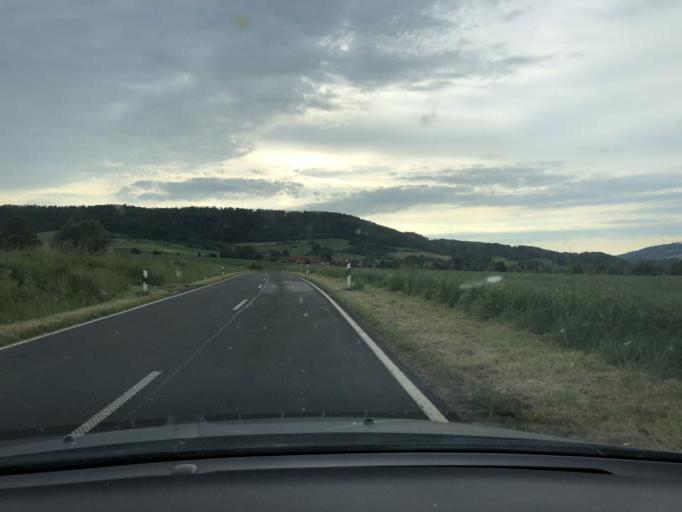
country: DE
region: Hesse
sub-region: Regierungsbezirk Kassel
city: Alheim
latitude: 51.0445
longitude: 9.6363
